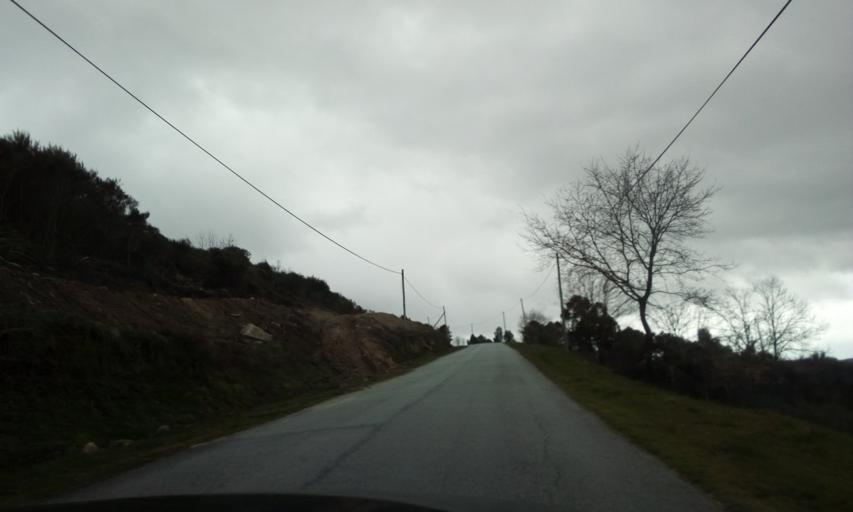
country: PT
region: Guarda
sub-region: Fornos de Algodres
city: Fornos de Algodres
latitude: 40.6368
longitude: -7.6027
